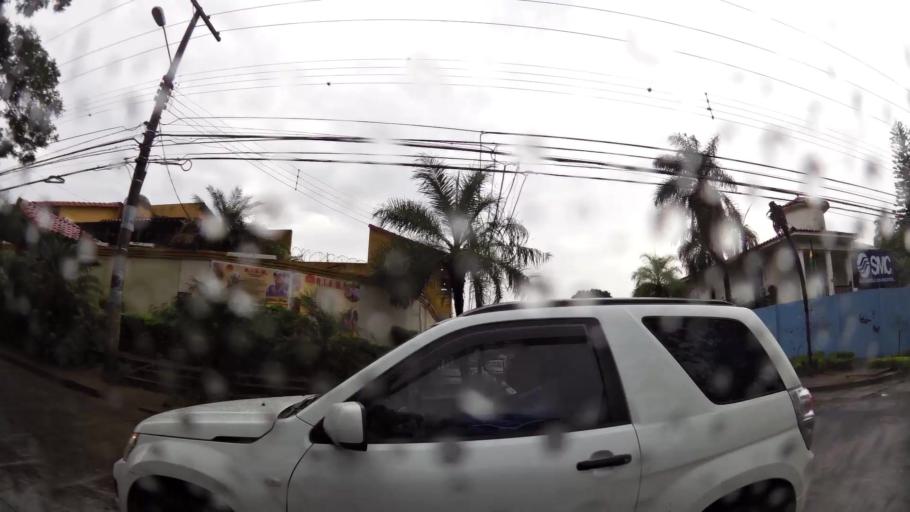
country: BO
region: Santa Cruz
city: Santa Cruz de la Sierra
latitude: -17.7768
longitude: -63.1573
